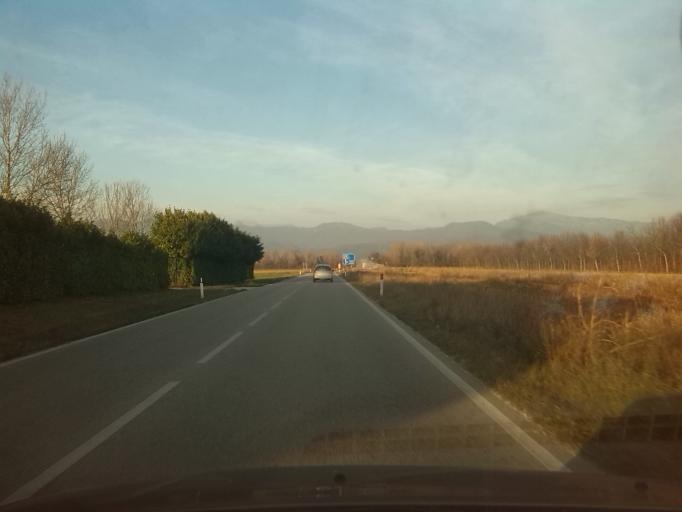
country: IT
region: Friuli Venezia Giulia
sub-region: Provincia di Udine
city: Cividale del Friuli
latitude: 46.0688
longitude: 13.4191
